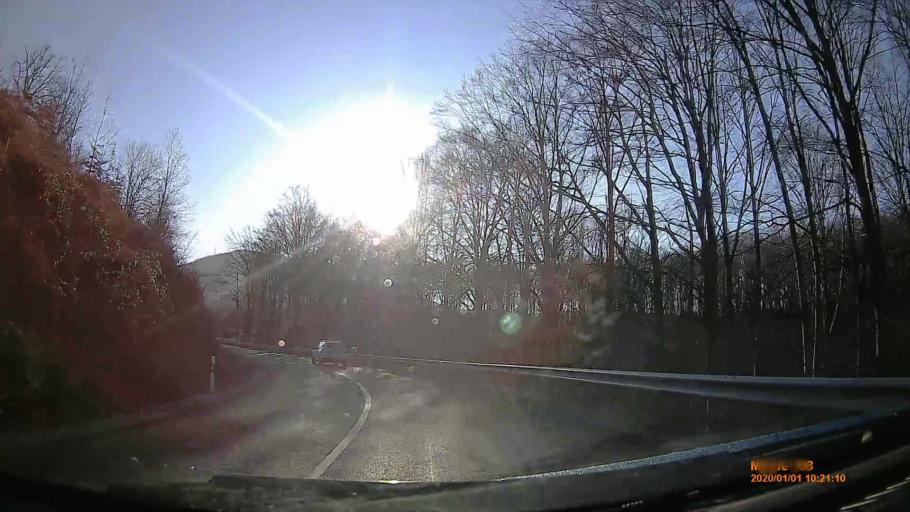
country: HU
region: Heves
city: Paradsasvar
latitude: 47.8967
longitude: 19.9835
